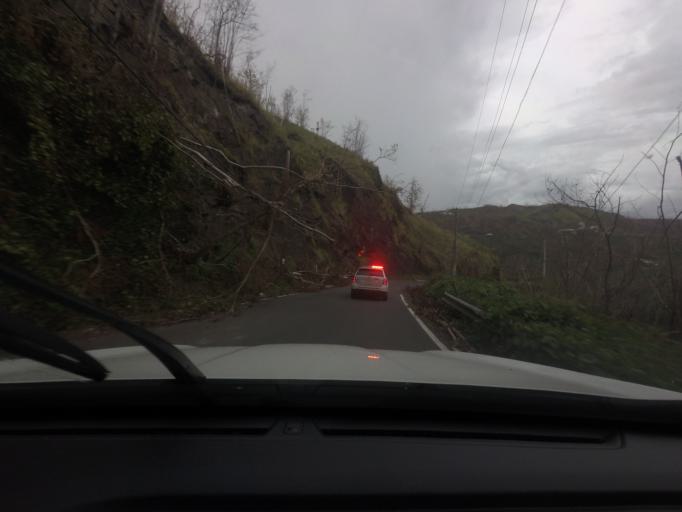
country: PR
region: Ciales
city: Ciales
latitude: 18.2883
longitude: -66.4825
